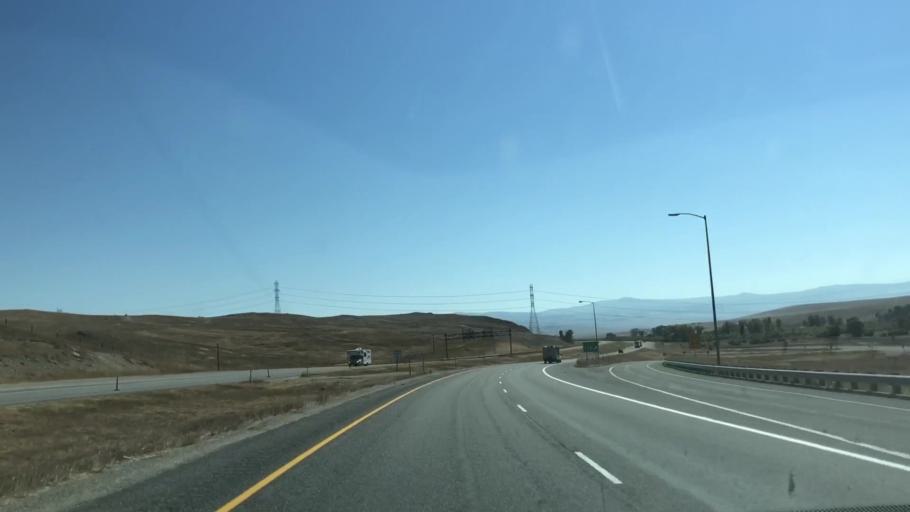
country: US
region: Montana
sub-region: Powell County
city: Deer Lodge
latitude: 46.5106
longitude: -112.7865
